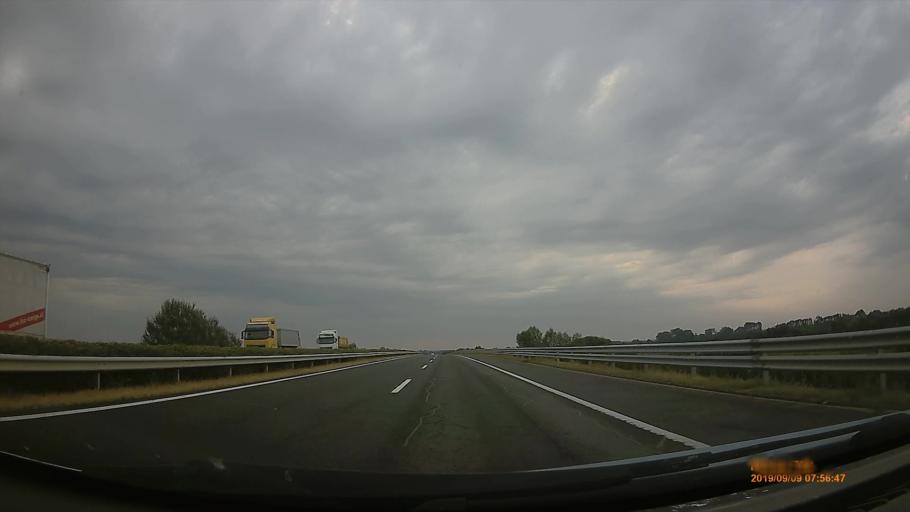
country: HU
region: Borsod-Abauj-Zemplen
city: Hejobaba
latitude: 47.8787
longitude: 20.9164
